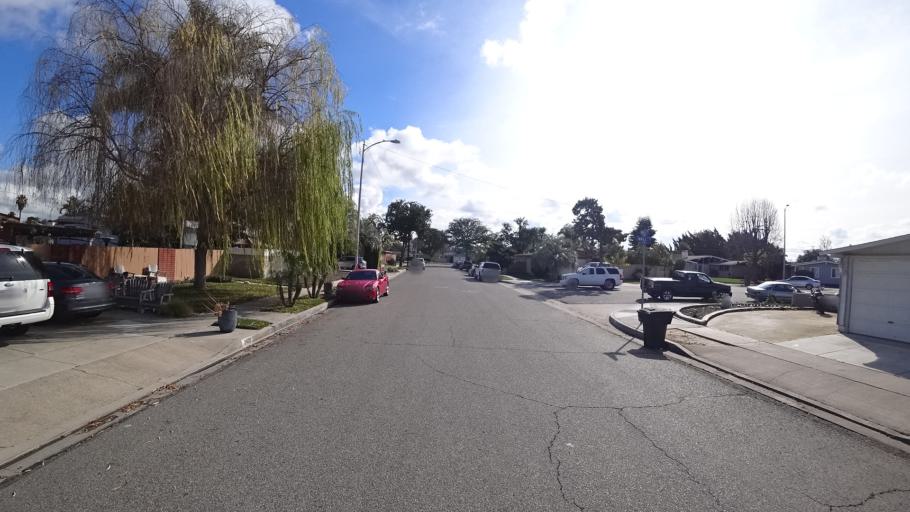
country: US
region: California
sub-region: Orange County
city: Stanton
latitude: 33.8297
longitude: -117.9697
